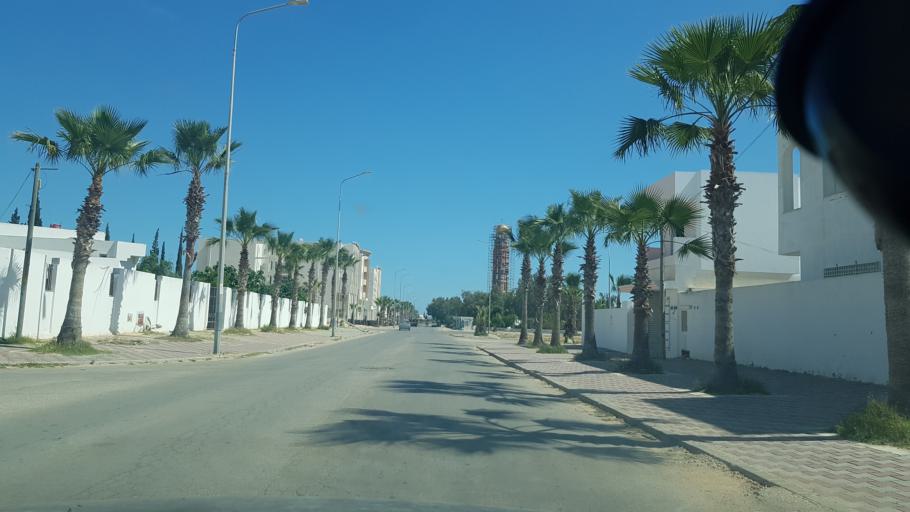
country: TN
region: Safaqis
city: Al Qarmadah
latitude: 34.8290
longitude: 10.7578
